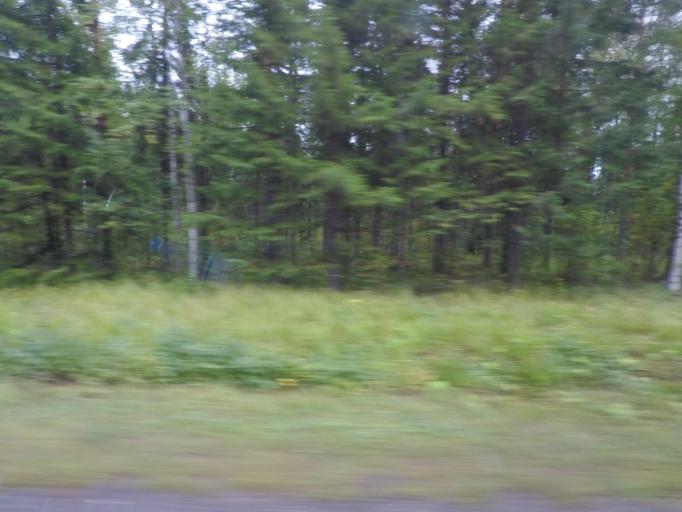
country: FI
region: Southern Savonia
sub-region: Pieksaemaeki
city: Joroinen
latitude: 62.1261
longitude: 27.8394
